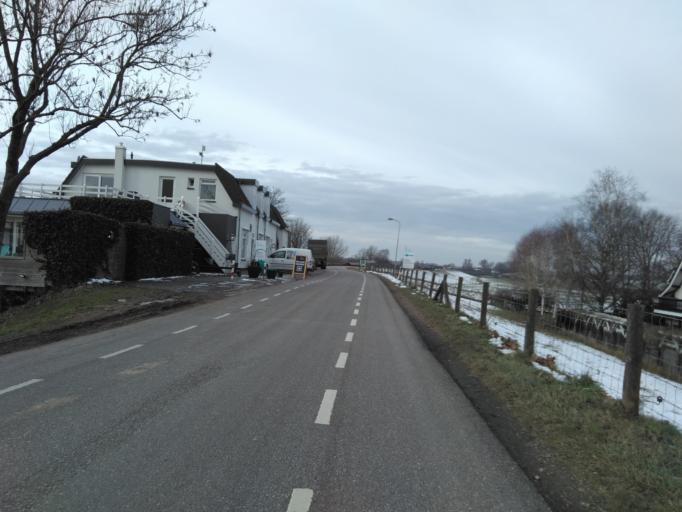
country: NL
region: Gelderland
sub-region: Gemeente Overbetuwe
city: Oosterhout
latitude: 51.8756
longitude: 5.8086
